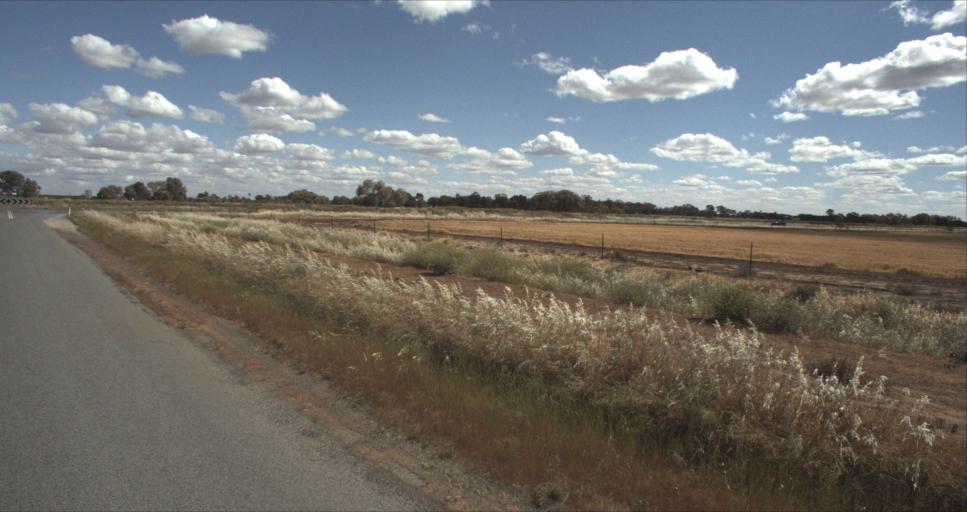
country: AU
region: New South Wales
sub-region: Leeton
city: Leeton
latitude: -34.5033
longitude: 146.2450
